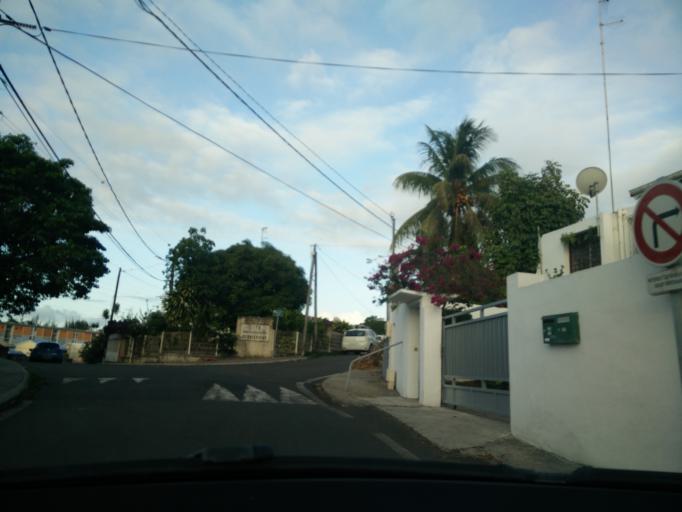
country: GP
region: Guadeloupe
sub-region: Guadeloupe
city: Pointe-a-Pitre
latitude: 16.2543
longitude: -61.5195
